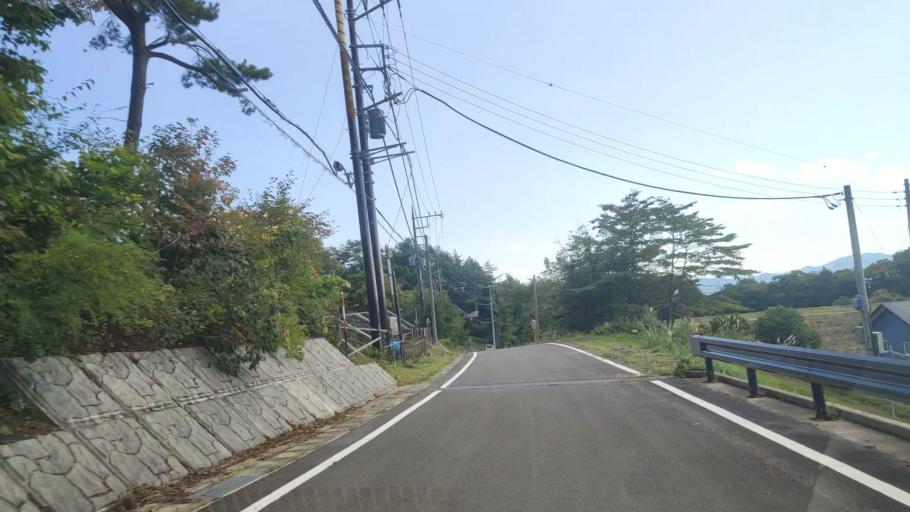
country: JP
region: Gunma
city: Nakanojomachi
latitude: 36.6424
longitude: 138.6204
